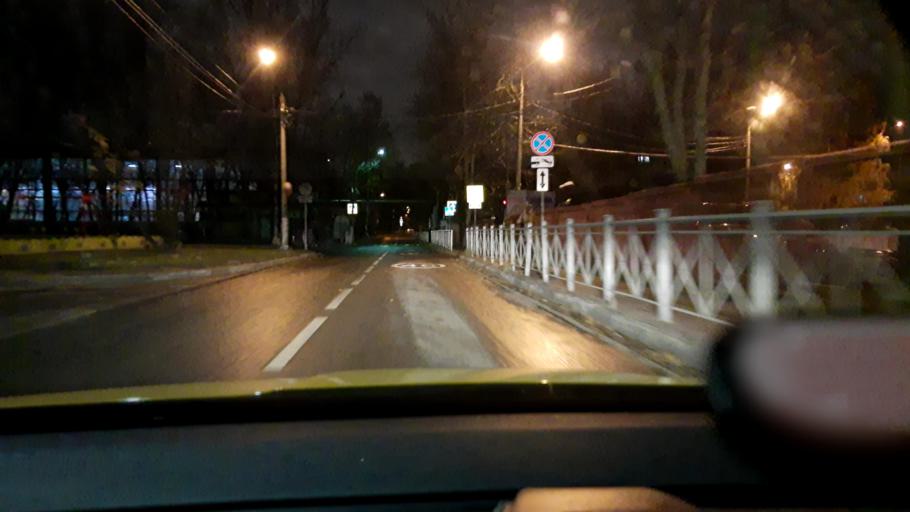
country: RU
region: Moscow
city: Khimki
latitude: 55.8915
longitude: 37.4224
